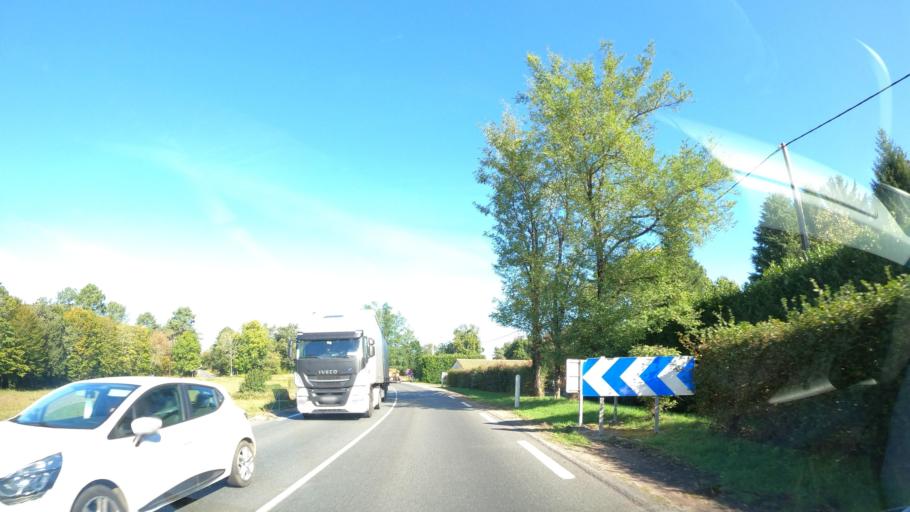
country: FR
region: Aquitaine
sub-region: Departement de la Dordogne
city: Notre-Dame-de-Sanilhac
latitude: 45.0995
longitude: 0.6956
